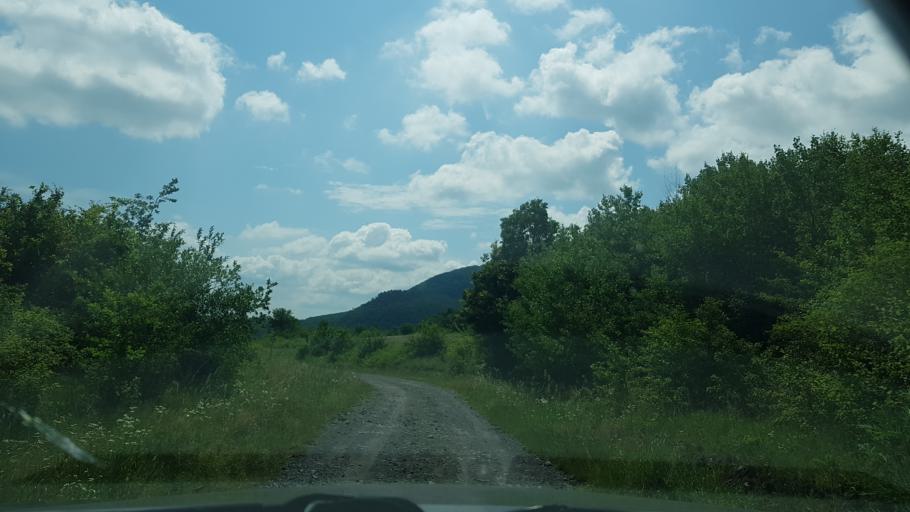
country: SK
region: Kosicky
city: Secovce
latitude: 48.5539
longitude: 21.4939
